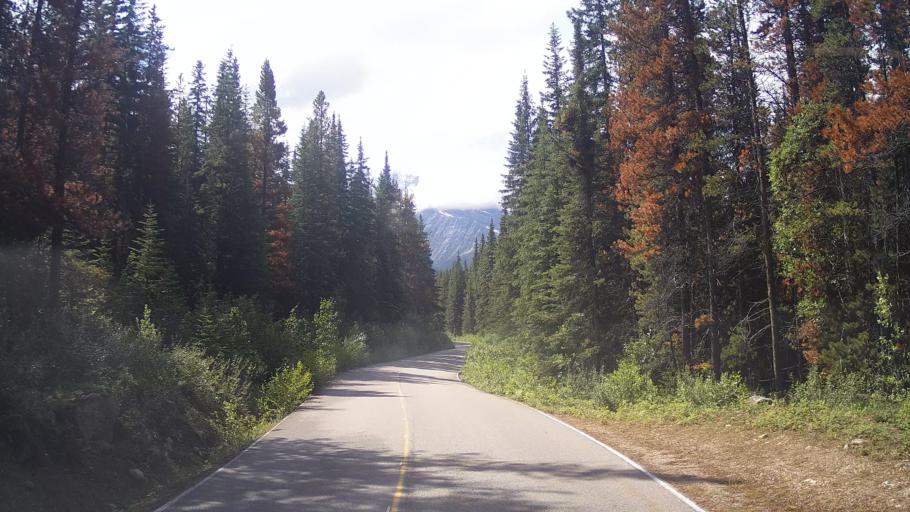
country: CA
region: Alberta
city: Jasper Park Lodge
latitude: 52.7569
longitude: -118.0436
